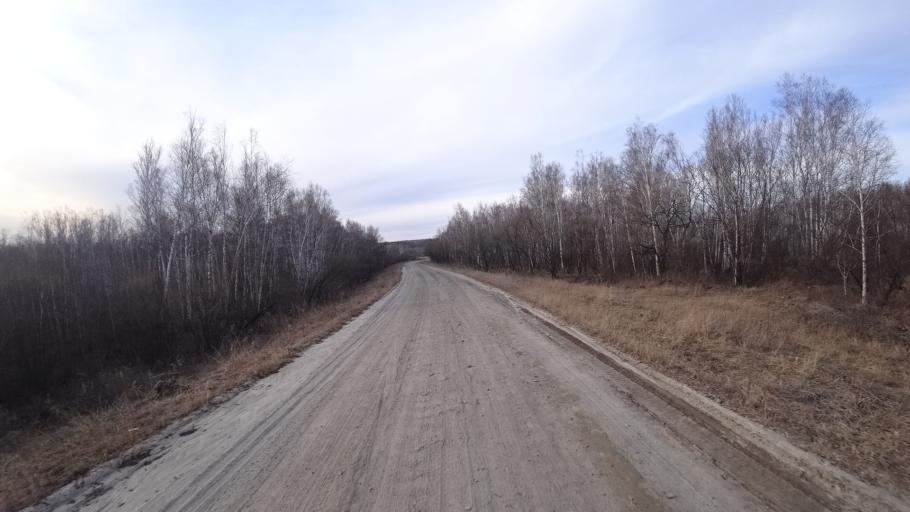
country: RU
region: Amur
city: Bureya
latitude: 50.0152
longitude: 129.7743
